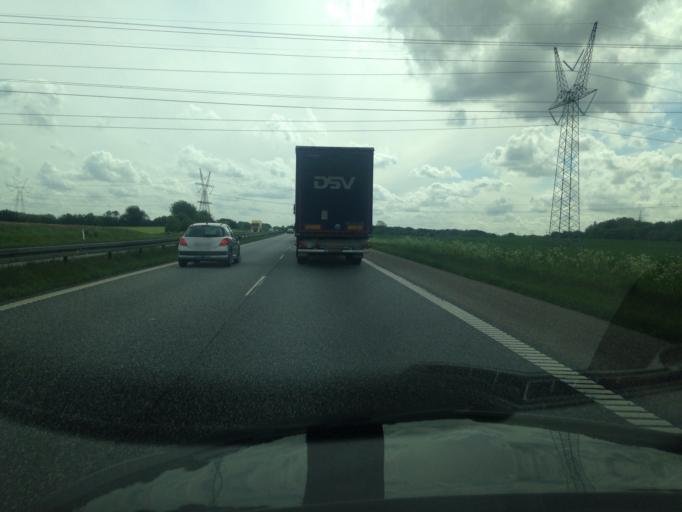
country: DK
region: South Denmark
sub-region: Fredericia Kommune
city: Taulov
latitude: 55.5642
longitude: 9.5543
